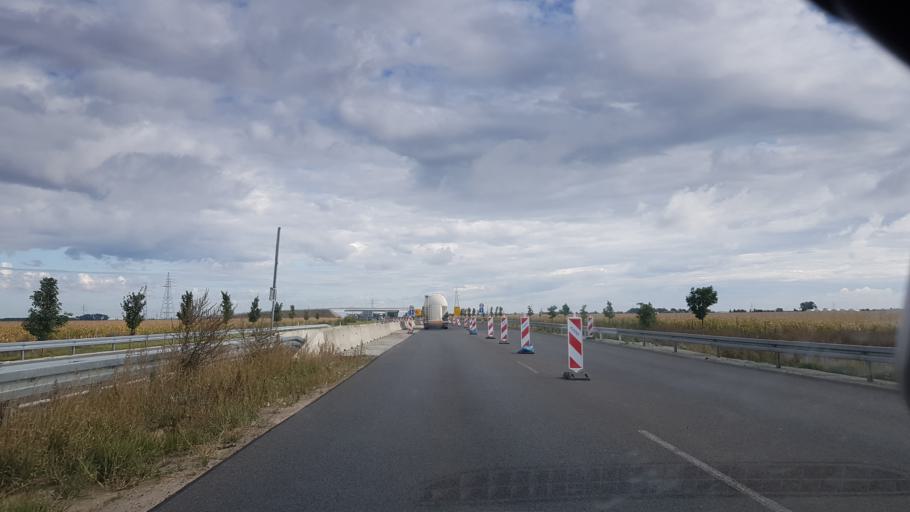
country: PL
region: Greater Poland Voivodeship
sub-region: Powiat poznanski
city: Komorniki
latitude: 52.3399
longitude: 16.7464
